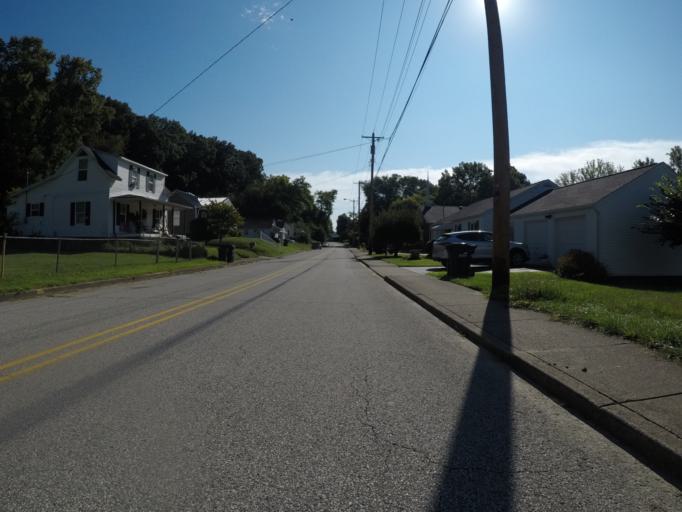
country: US
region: Kentucky
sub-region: Boyd County
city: Ashland
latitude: 38.4550
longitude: -82.6193
